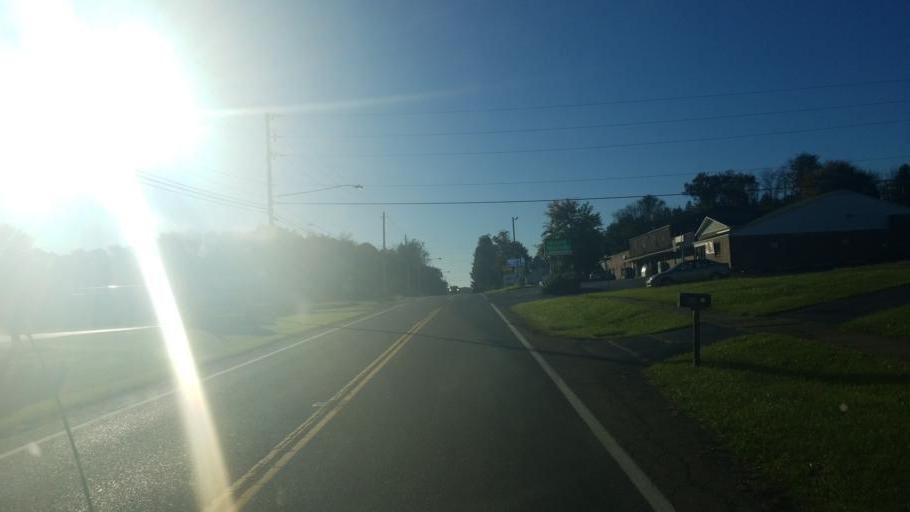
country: US
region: Ohio
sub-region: Columbiana County
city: Leetonia
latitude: 40.9007
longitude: -80.7739
